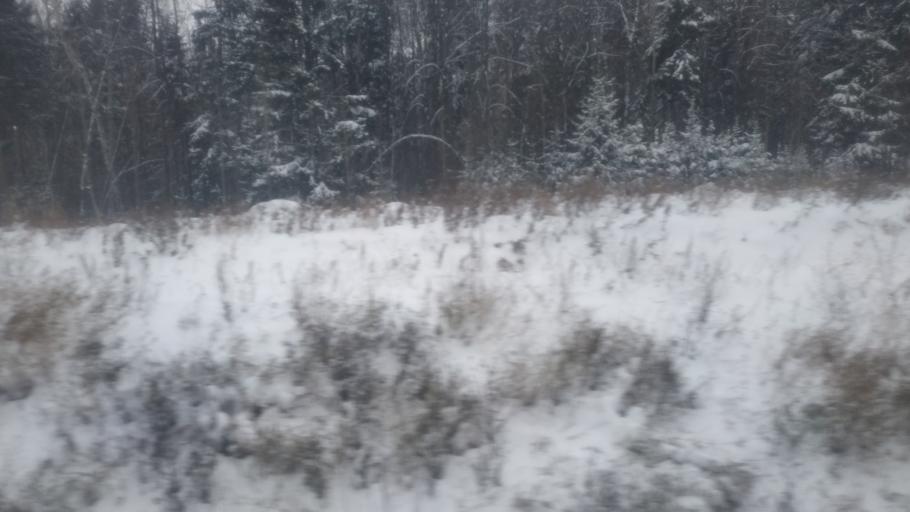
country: RU
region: Udmurtiya
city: Malaya Purga
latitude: 56.5509
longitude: 53.0973
